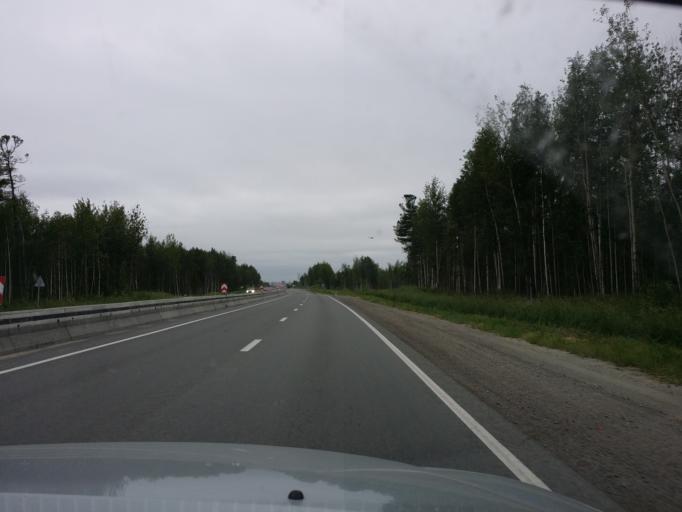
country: RU
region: Khanty-Mansiyskiy Avtonomnyy Okrug
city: Megion
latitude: 61.0586
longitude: 76.1609
